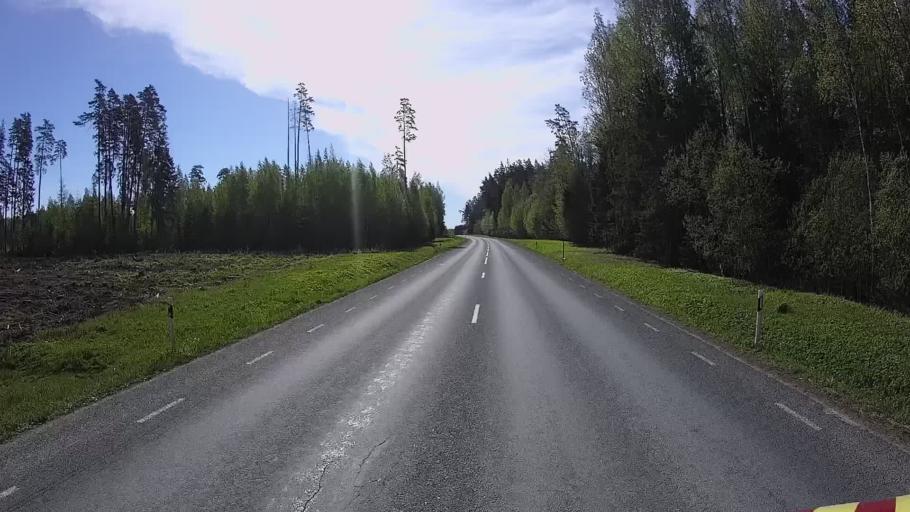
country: EE
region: Polvamaa
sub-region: Polva linn
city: Polva
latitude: 58.1649
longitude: 27.1502
